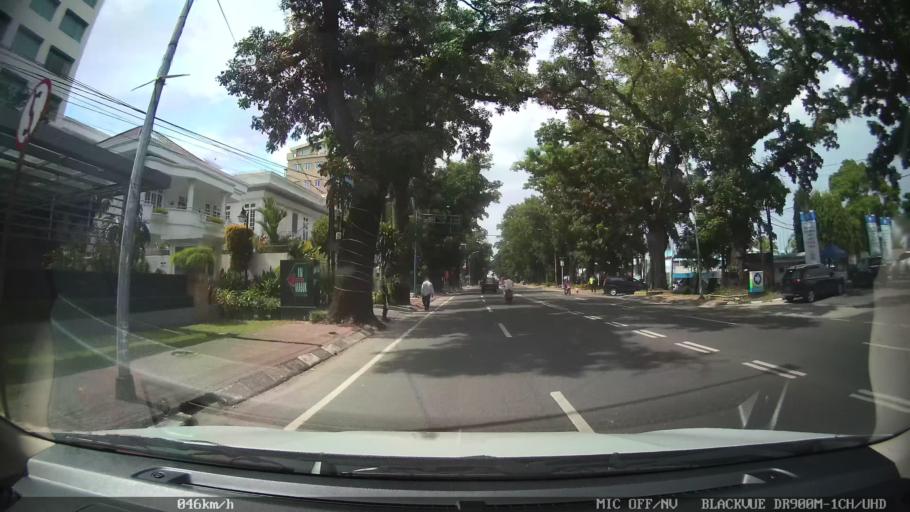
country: ID
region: North Sumatra
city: Medan
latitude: 3.6020
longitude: 98.6732
